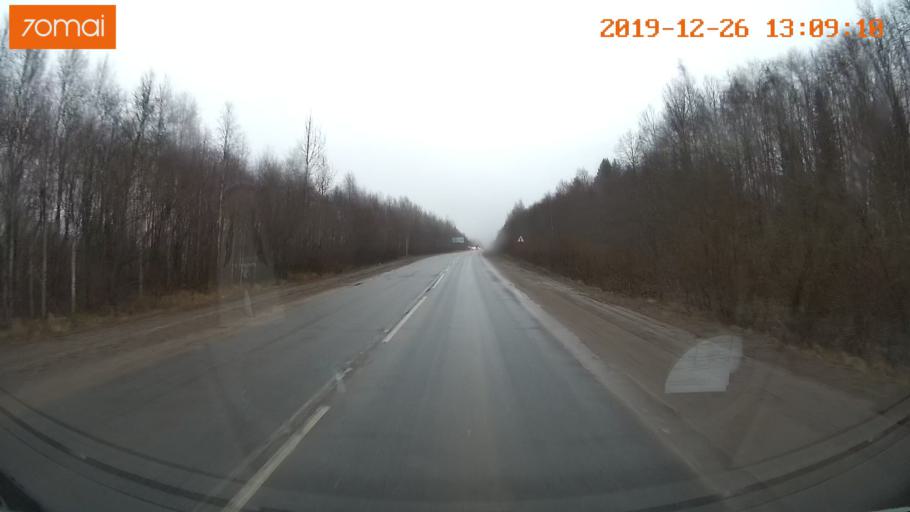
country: RU
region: Vologda
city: Cherepovets
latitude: 59.0500
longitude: 37.9519
